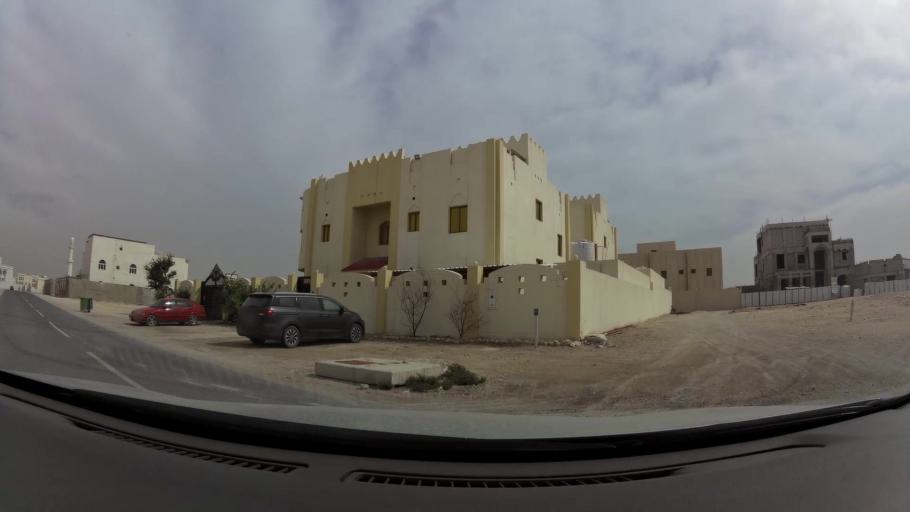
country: QA
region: Baladiyat ad Dawhah
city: Doha
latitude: 25.2174
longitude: 51.4851
